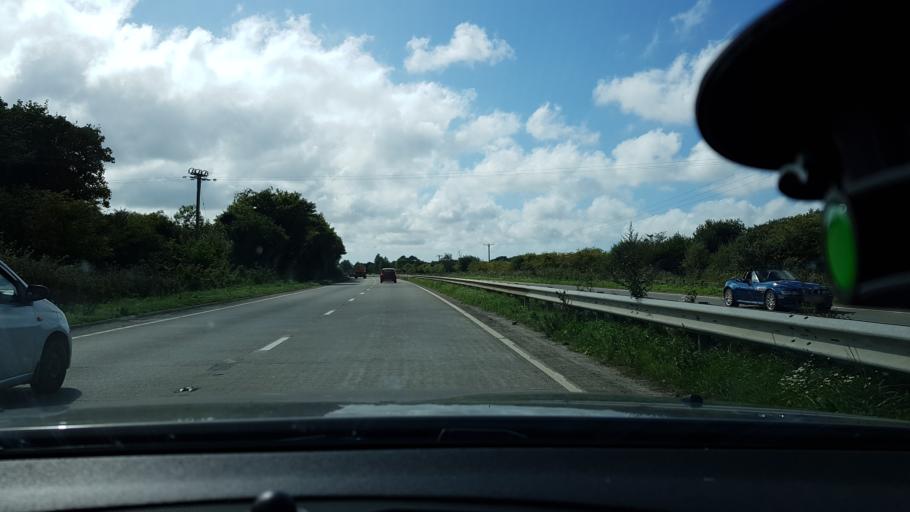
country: GB
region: England
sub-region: Cornwall
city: Marazion
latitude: 50.1335
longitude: -5.4979
